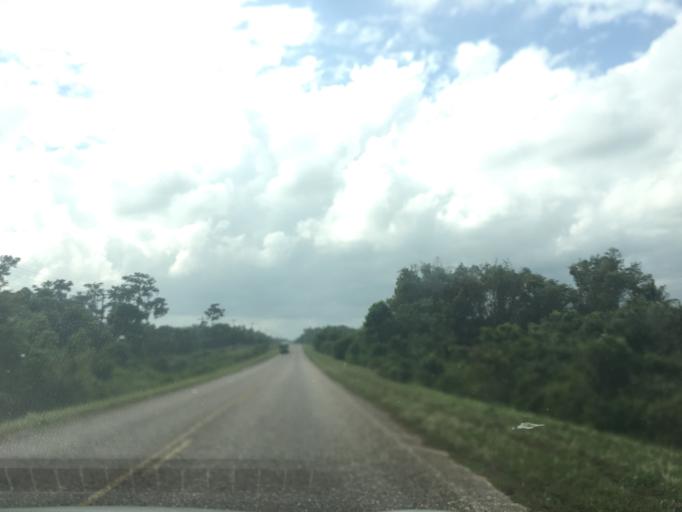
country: BZ
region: Stann Creek
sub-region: Dangriga
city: Dangriga
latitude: 16.9693
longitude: -88.3049
